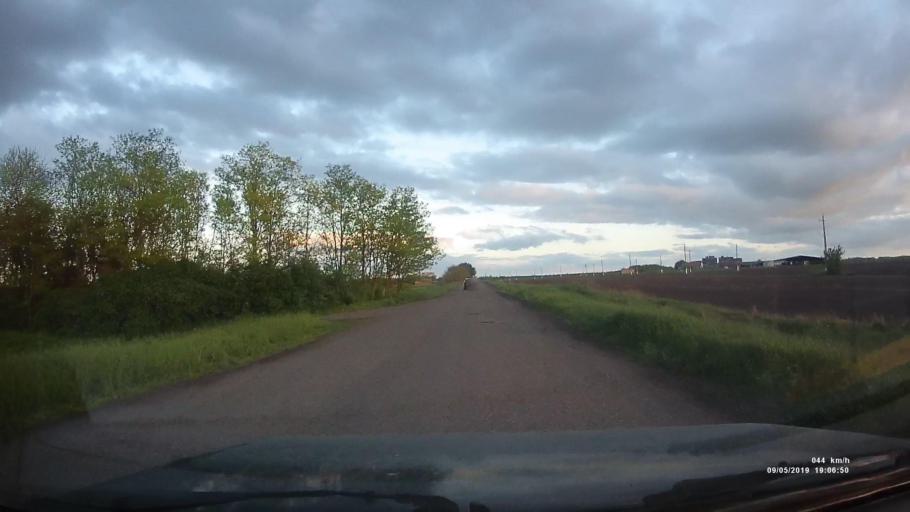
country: RU
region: Krasnodarskiy
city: Kanelovskaya
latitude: 46.7381
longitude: 39.1953
